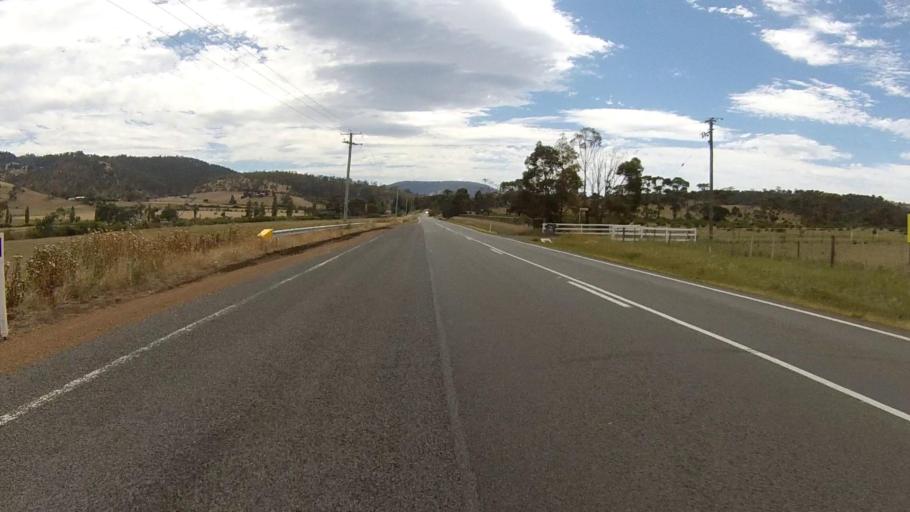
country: AU
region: Tasmania
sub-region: Brighton
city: Old Beach
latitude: -42.6761
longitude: 147.3571
